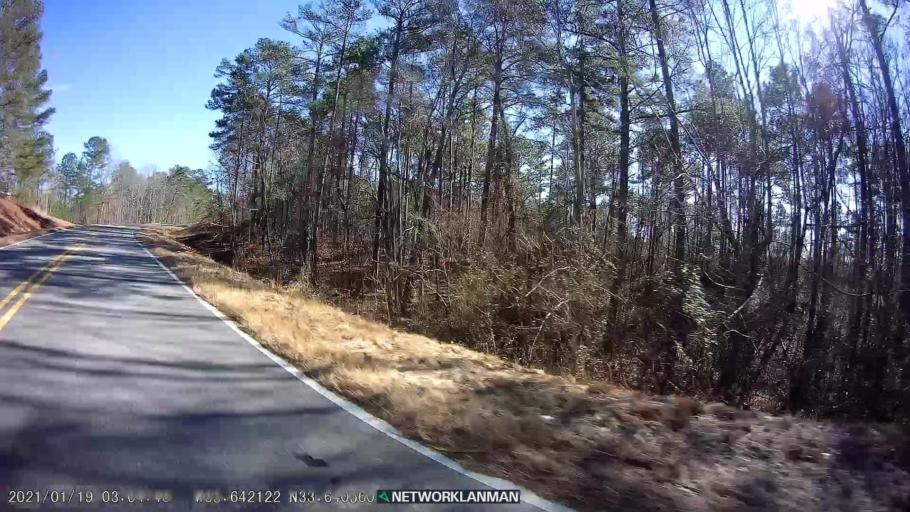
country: US
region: Alabama
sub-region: Cleburne County
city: Heflin
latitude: 33.6404
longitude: -85.6418
